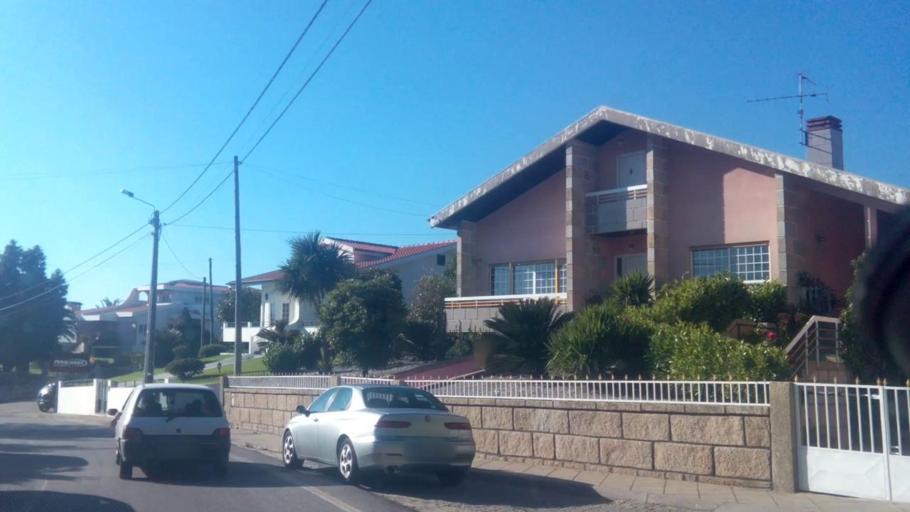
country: PT
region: Porto
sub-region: Penafiel
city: Penafiel
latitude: 41.1950
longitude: -8.2726
